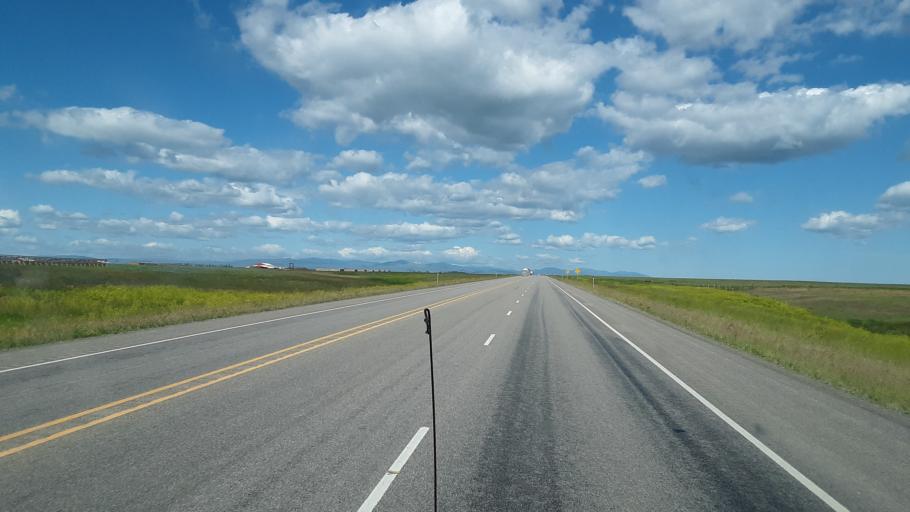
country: US
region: Montana
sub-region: Fergus County
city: Lewistown
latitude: 46.9985
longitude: -109.8122
